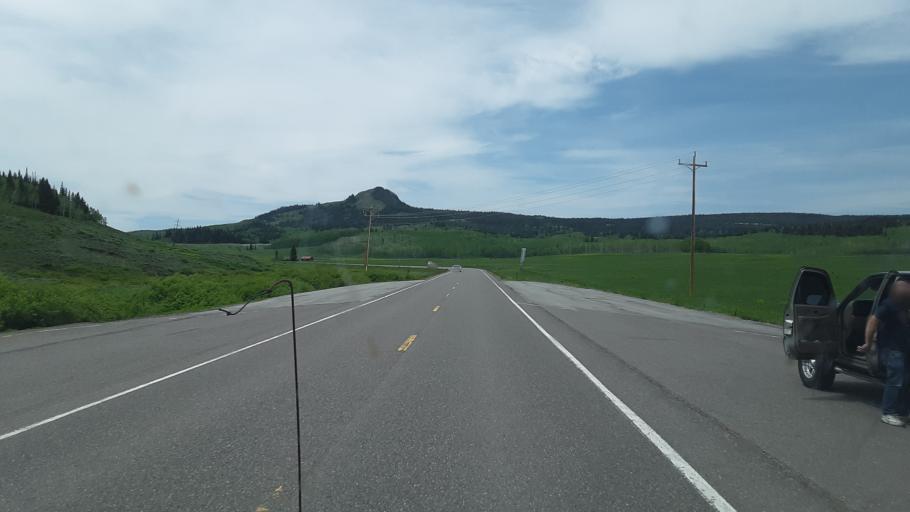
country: US
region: Colorado
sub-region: Routt County
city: Steamboat Springs
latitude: 40.3934
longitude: -106.5645
